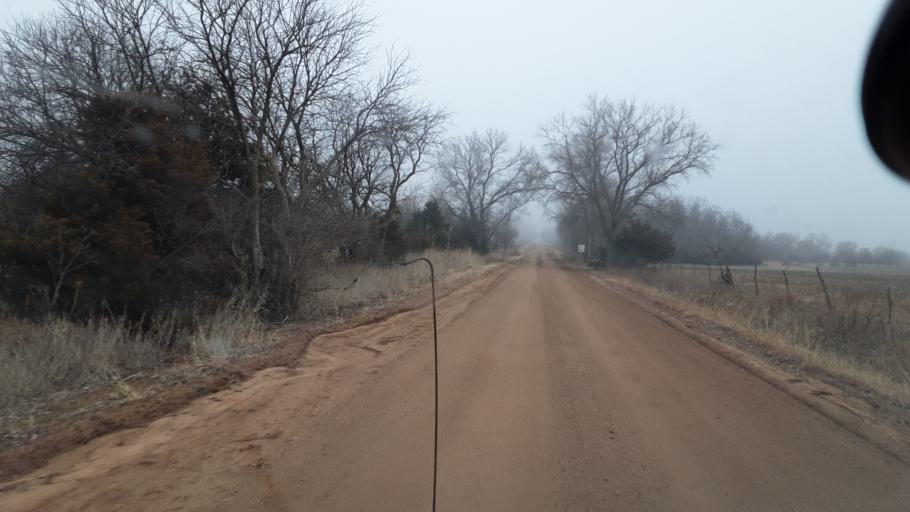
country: US
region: Kansas
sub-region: Reno County
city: South Hutchinson
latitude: 37.9079
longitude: -97.9954
